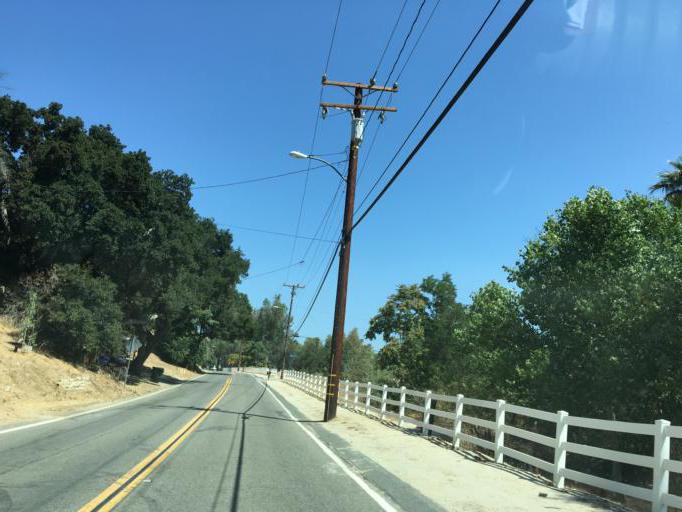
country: US
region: California
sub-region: Los Angeles County
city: Val Verde
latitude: 34.4425
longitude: -118.6571
